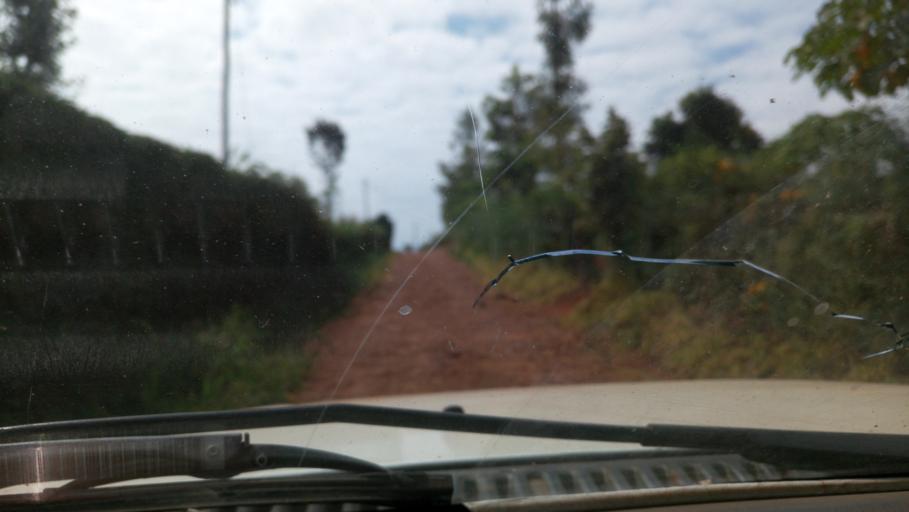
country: KE
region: Murang'a District
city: Murang'a
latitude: -0.6350
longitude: 37.0746
